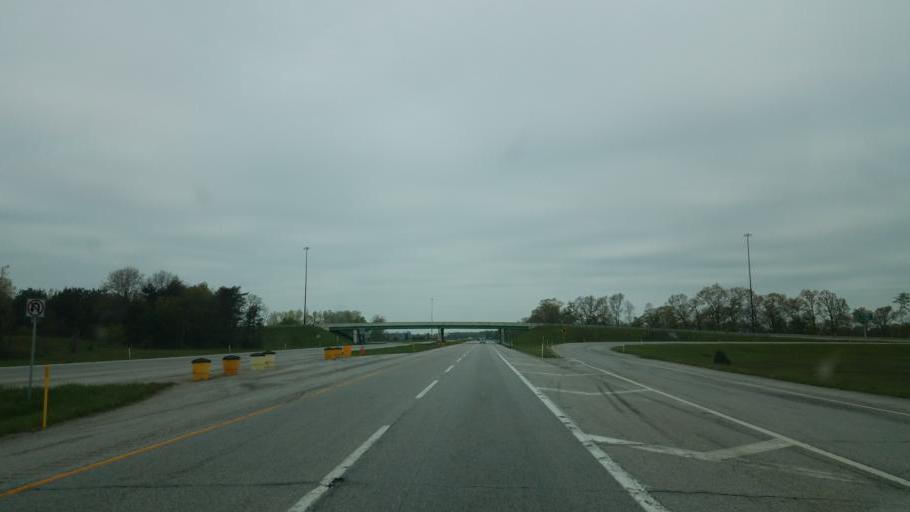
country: US
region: Michigan
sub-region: Saint Joseph County
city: White Pigeon
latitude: 41.7473
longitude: -85.6838
